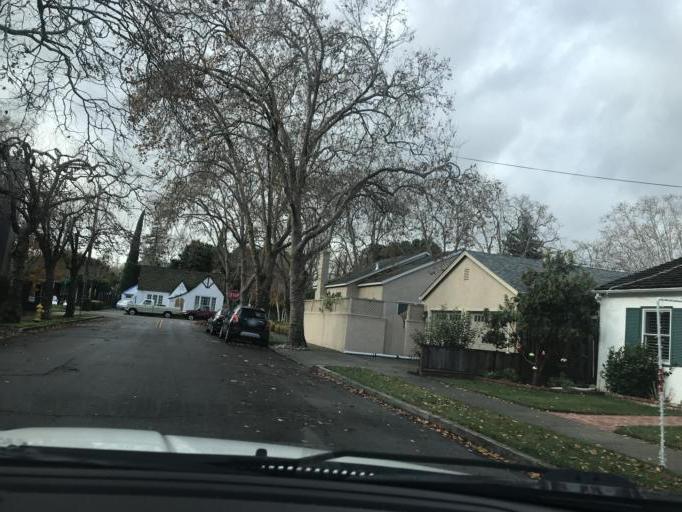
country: US
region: California
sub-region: Santa Clara County
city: Buena Vista
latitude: 37.3089
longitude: -121.9054
